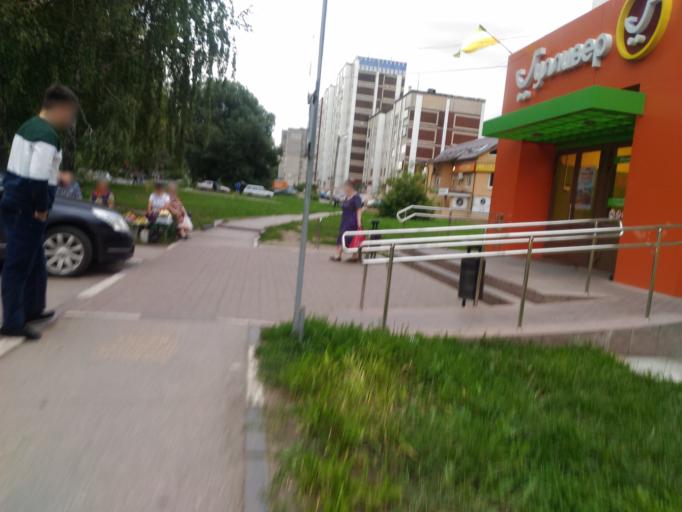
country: RU
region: Ulyanovsk
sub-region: Ulyanovskiy Rayon
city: Ulyanovsk
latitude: 54.2634
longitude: 48.3295
